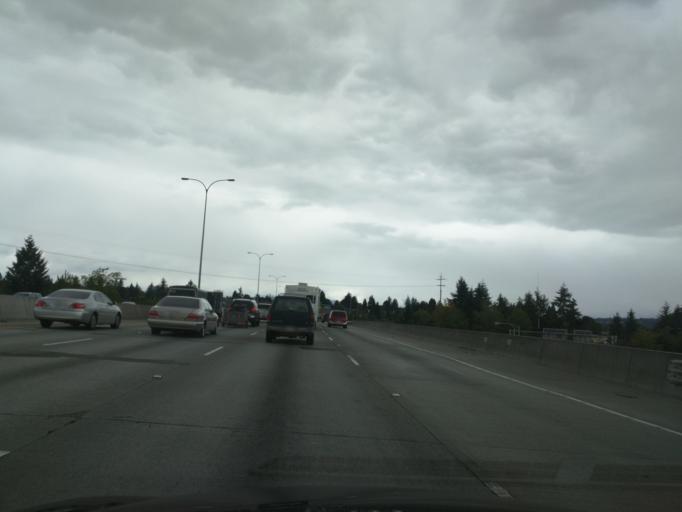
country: US
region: Washington
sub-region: Snohomish County
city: Everett
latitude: 47.9805
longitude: -122.1884
